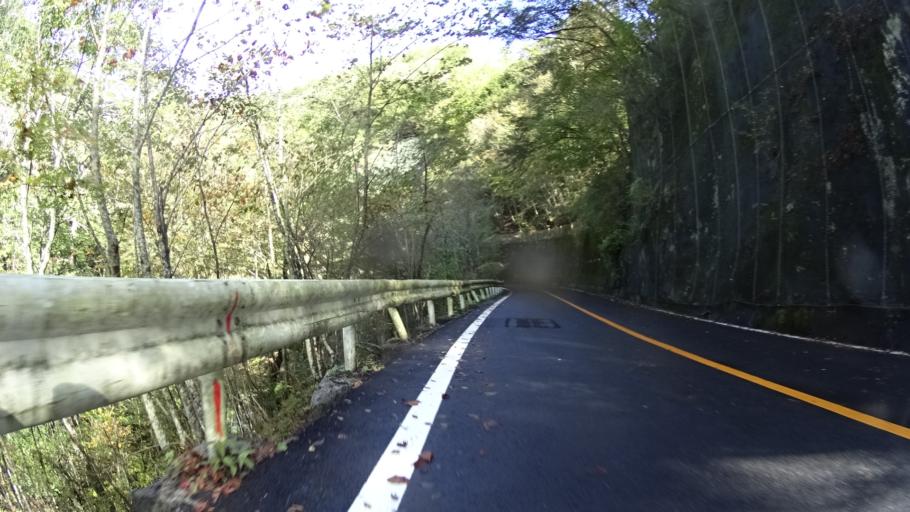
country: JP
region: Yamanashi
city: Enzan
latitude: 35.8028
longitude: 138.8519
